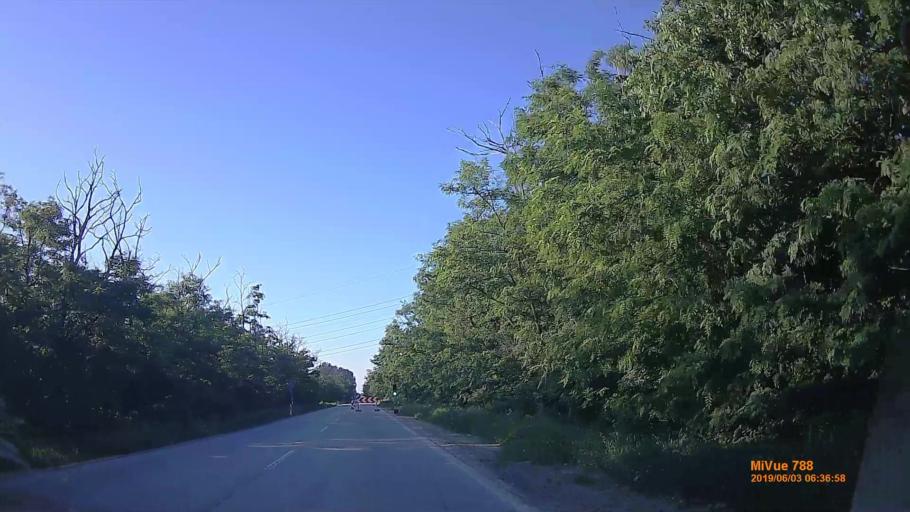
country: HU
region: Pest
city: Taksony
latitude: 47.3044
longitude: 19.0846
